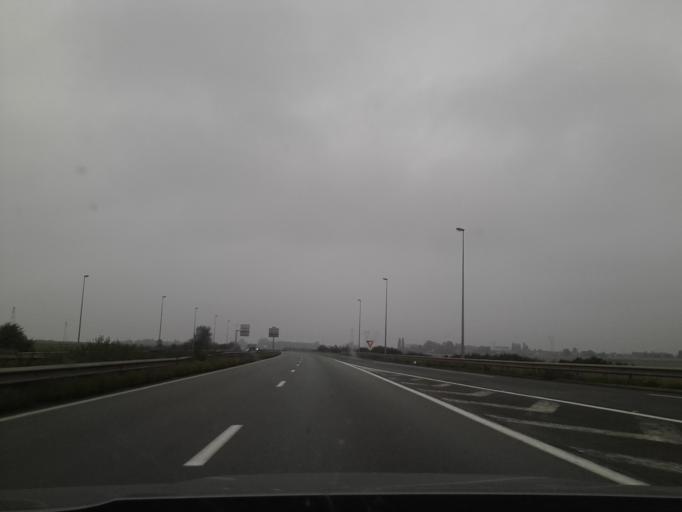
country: FR
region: Nord-Pas-de-Calais
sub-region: Departement du Nord
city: Douchy-les-Mines
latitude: 50.3017
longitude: 3.3715
